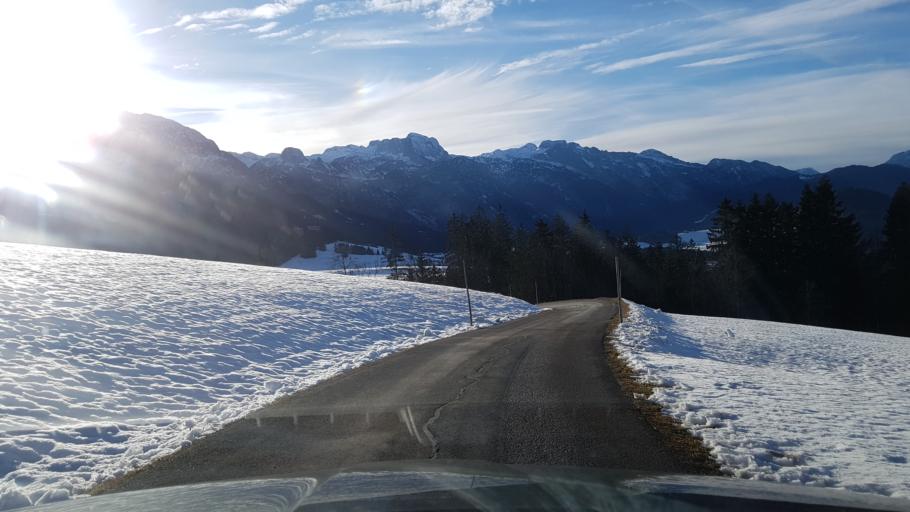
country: AT
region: Salzburg
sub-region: Politischer Bezirk Hallein
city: Abtenau
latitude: 47.5715
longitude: 13.4081
